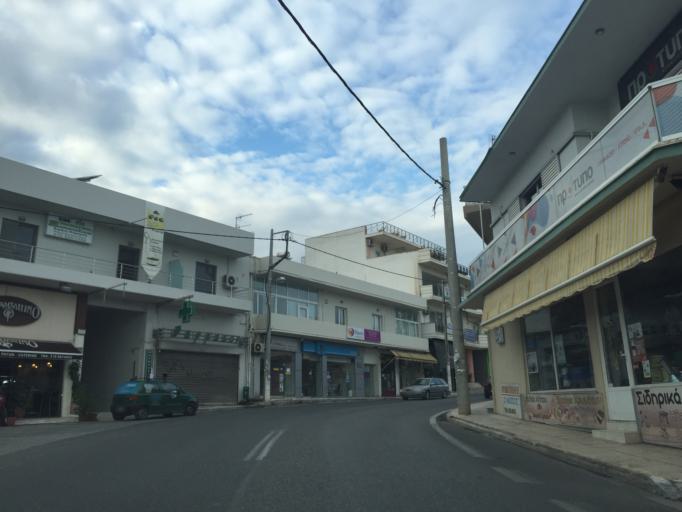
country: GR
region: Attica
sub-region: Nomarchia Anatolikis Attikis
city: Vari
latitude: 37.8313
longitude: 23.8027
